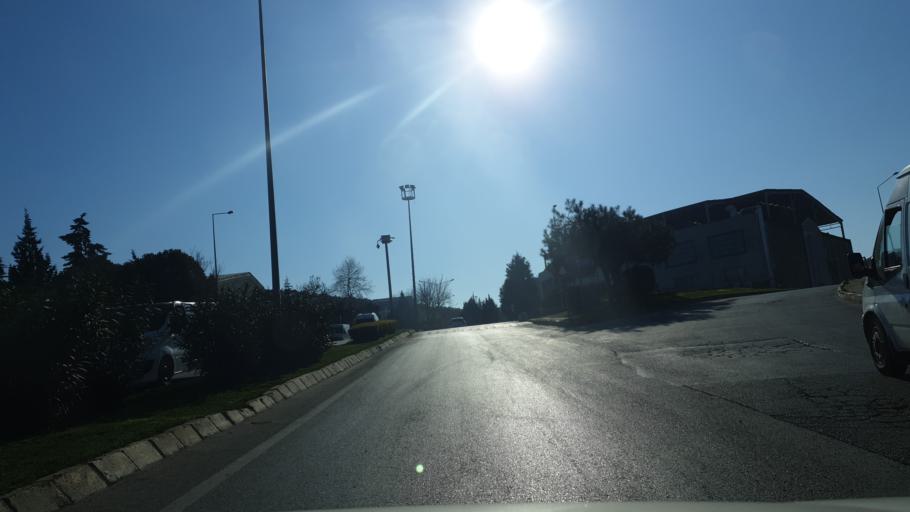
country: TR
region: Istanbul
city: Icmeler
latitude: 40.8799
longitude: 29.3544
